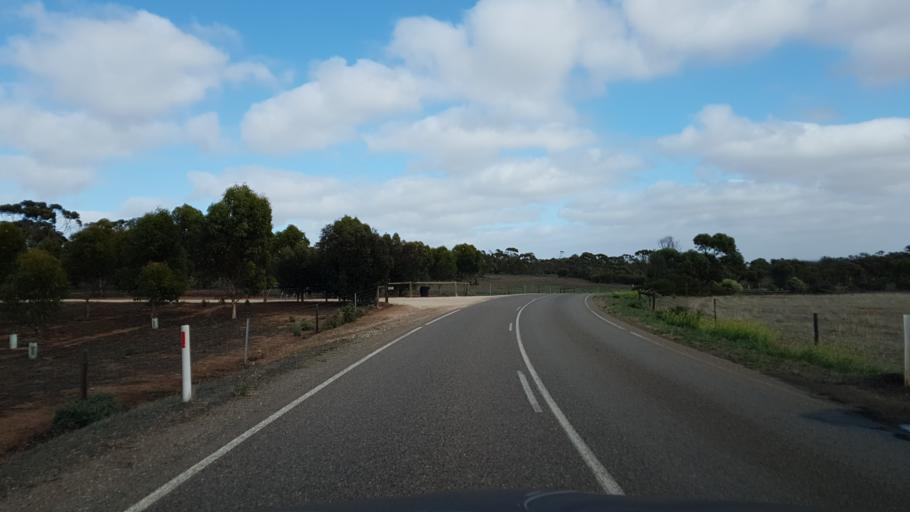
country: AU
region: South Australia
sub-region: Murray Bridge
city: Murray Bridge
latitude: -35.1147
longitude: 139.2143
